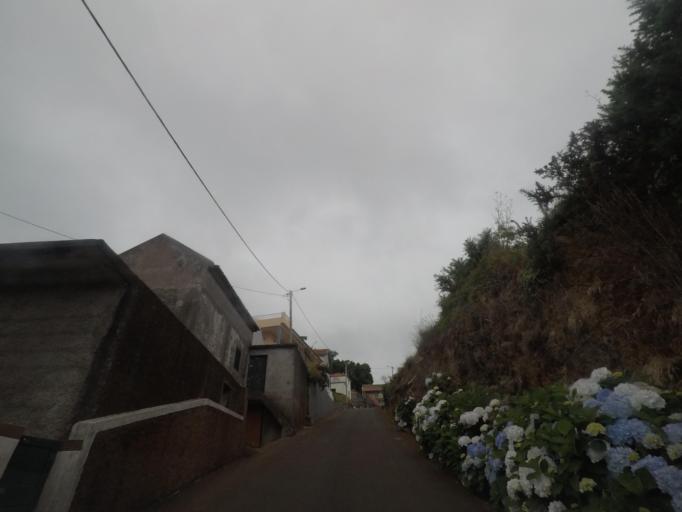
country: PT
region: Madeira
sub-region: Porto Moniz
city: Porto Moniz
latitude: 32.8583
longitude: -17.1982
